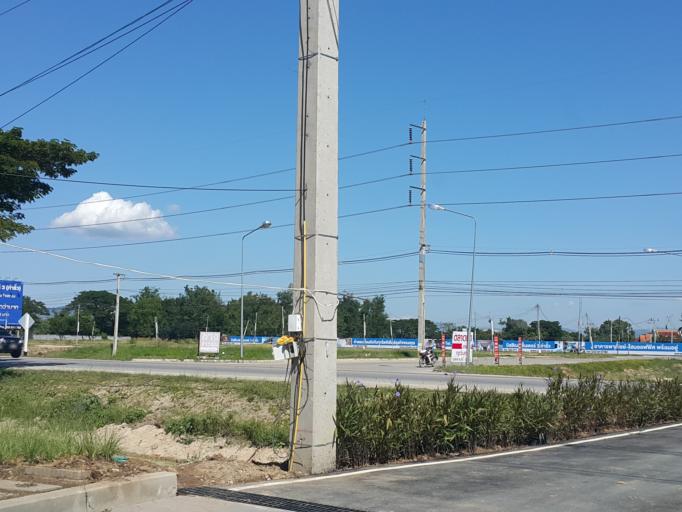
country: TH
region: Chiang Mai
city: San Sai
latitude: 18.8046
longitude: 99.0605
